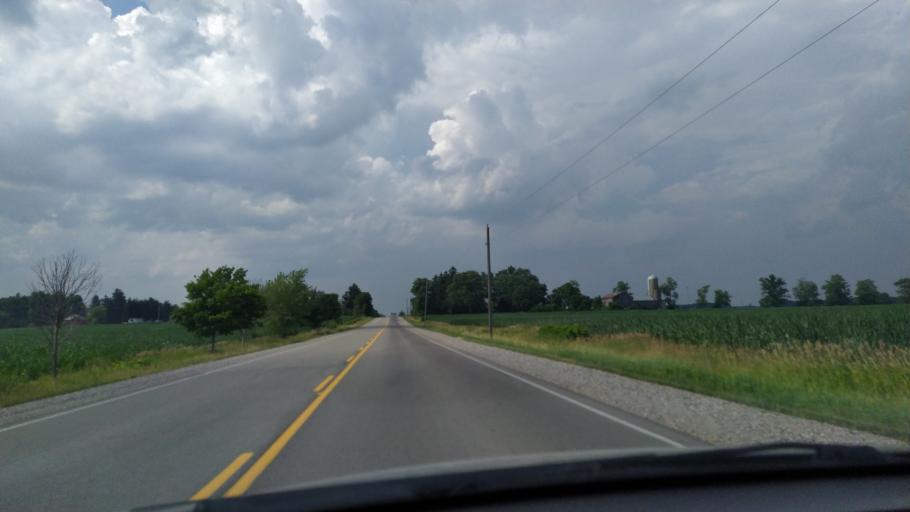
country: CA
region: Ontario
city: Dorchester
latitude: 43.0707
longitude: -81.1409
